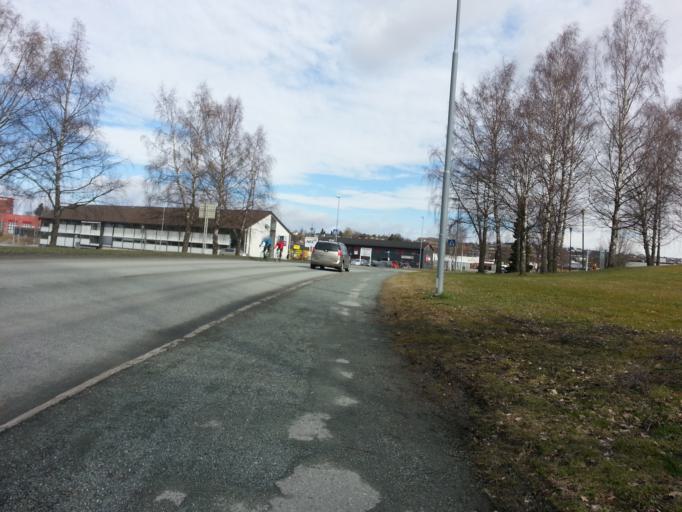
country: NO
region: Sor-Trondelag
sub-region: Trondheim
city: Trondheim
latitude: 63.3979
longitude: 10.3986
